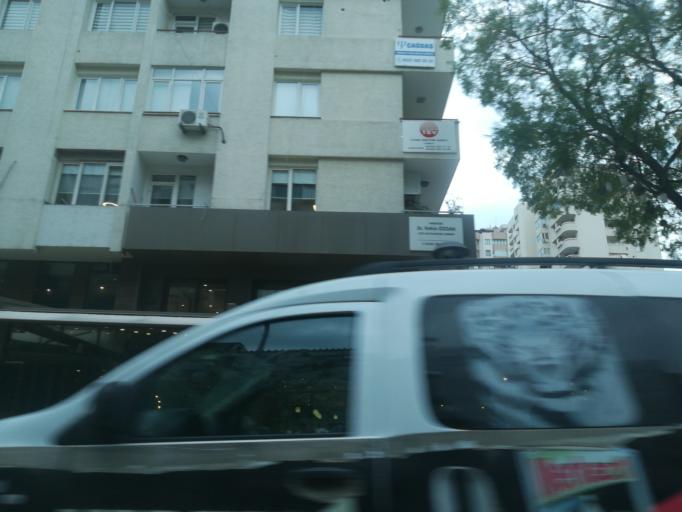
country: TR
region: Adana
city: Adana
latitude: 37.0007
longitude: 35.3204
